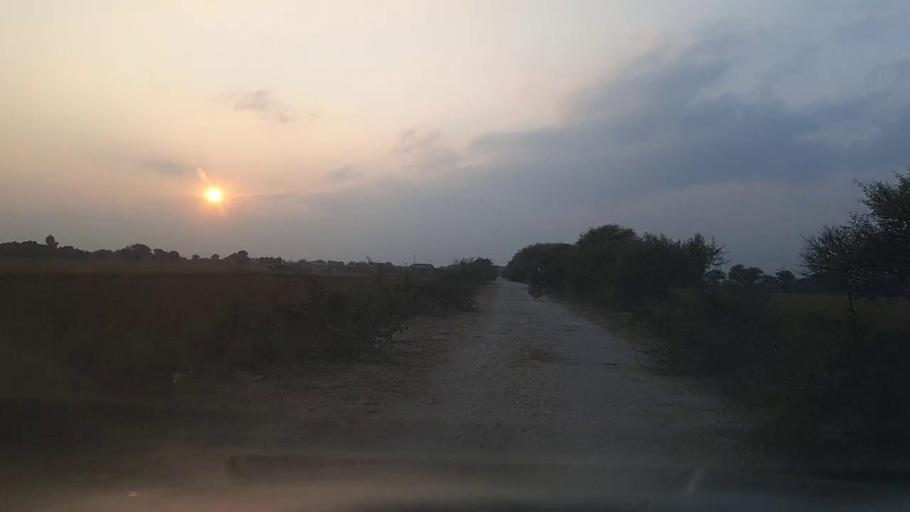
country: PK
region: Sindh
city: Jati
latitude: 24.5296
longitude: 68.3903
